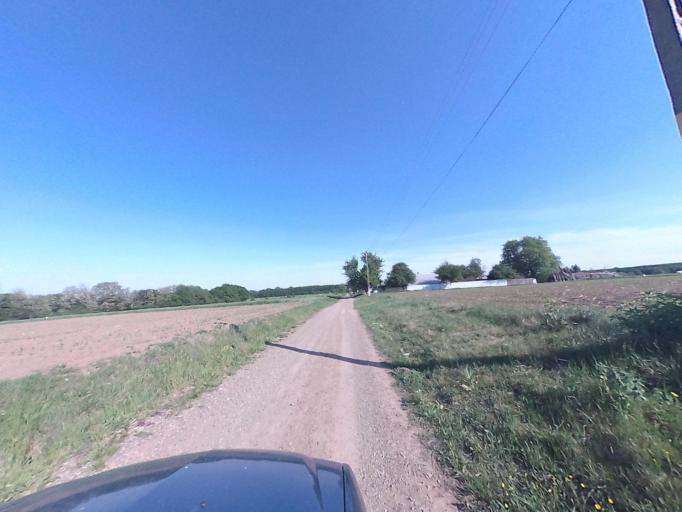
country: RO
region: Neamt
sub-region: Comuna Dulcesti
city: Dulcesti
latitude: 47.0009
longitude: 26.7771
